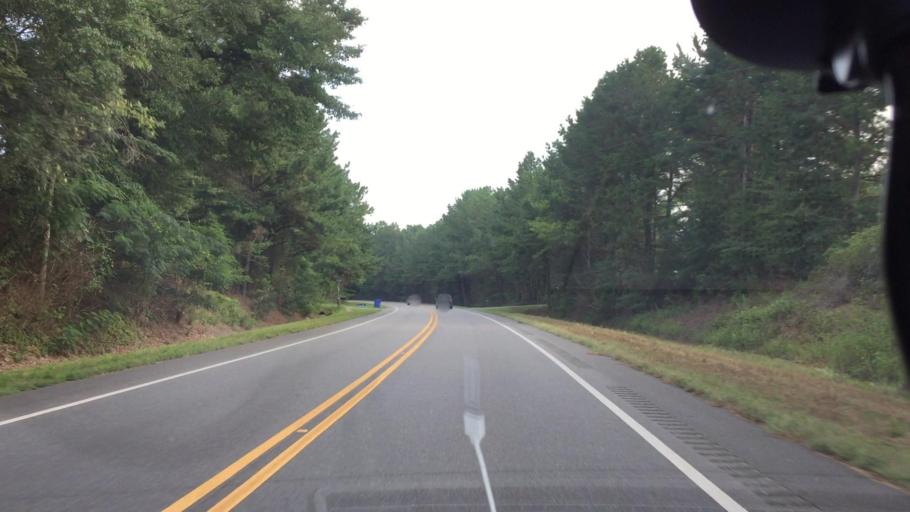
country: US
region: Alabama
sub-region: Pike County
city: Brundidge
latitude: 31.5977
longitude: -85.9466
